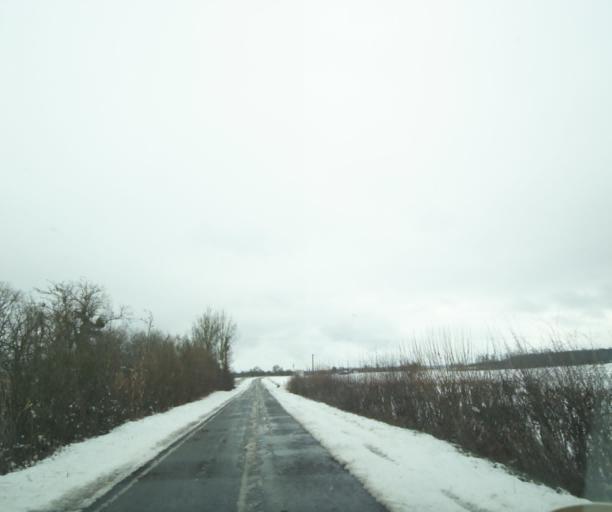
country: FR
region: Champagne-Ardenne
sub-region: Departement de la Haute-Marne
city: Montier-en-Der
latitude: 48.4195
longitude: 4.7311
